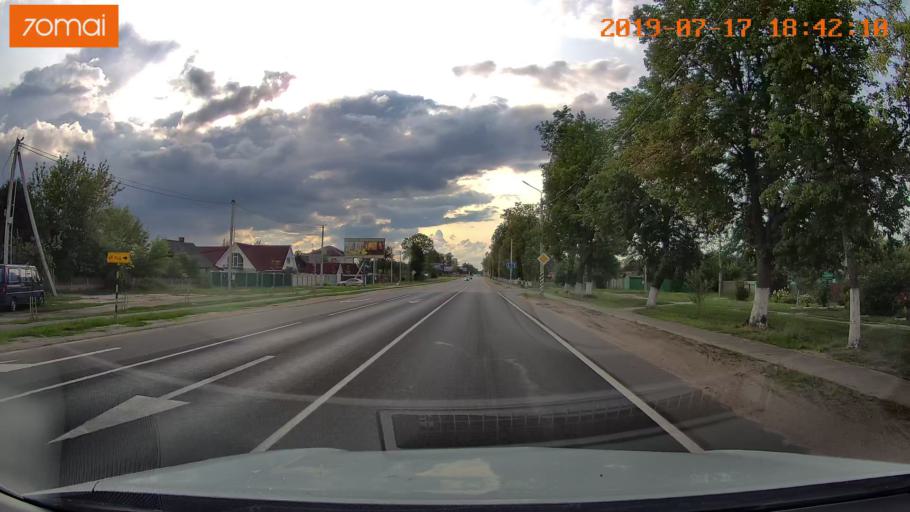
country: BY
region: Mogilev
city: Asipovichy
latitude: 53.3088
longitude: 28.6524
